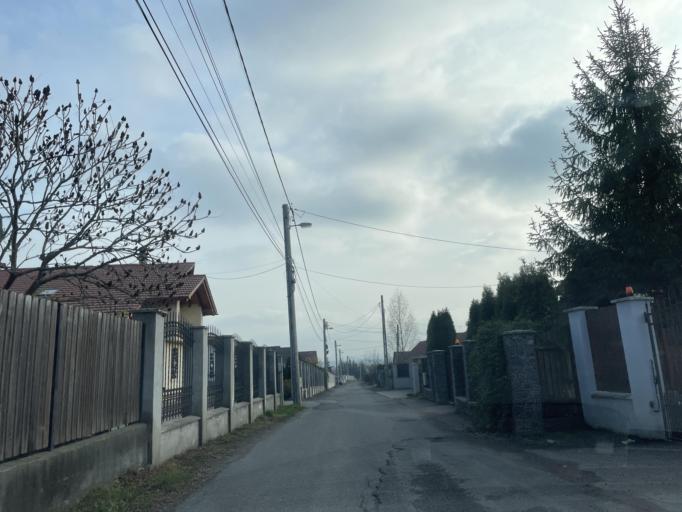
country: RO
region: Mures
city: Reghin-Sat
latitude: 46.7917
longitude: 24.7088
